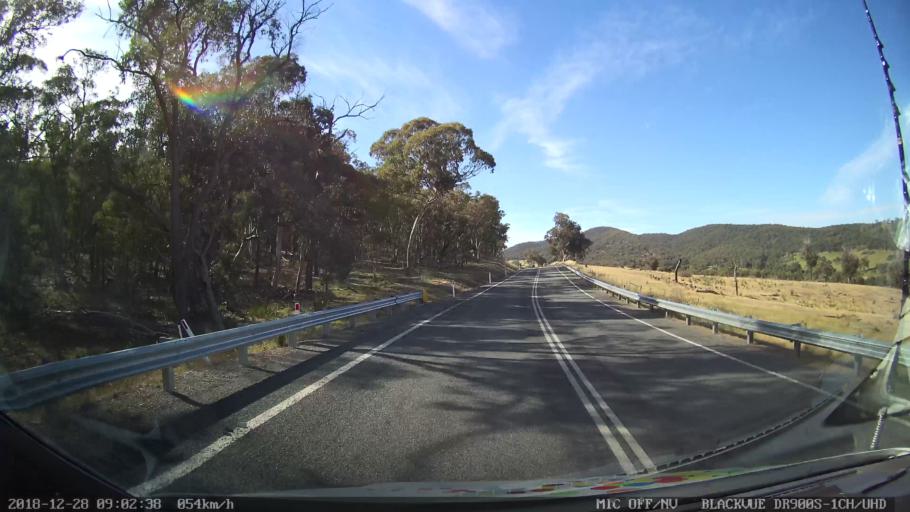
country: AU
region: New South Wales
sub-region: Upper Lachlan Shire
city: Crookwell
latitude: -34.1561
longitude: 149.3348
